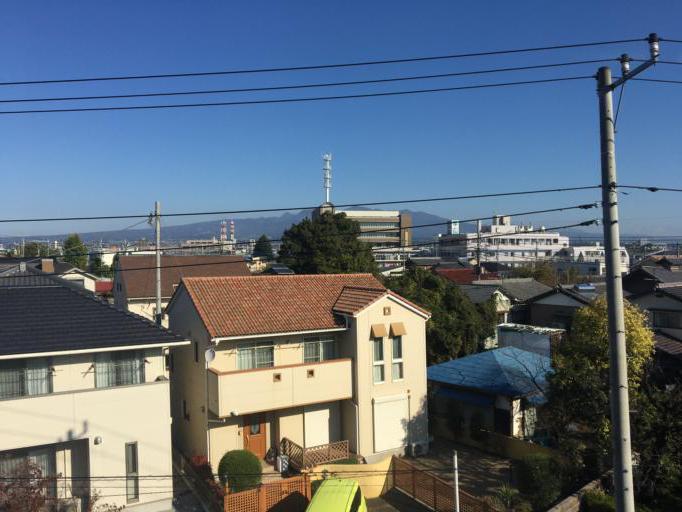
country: JP
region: Gunma
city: Maebashi-shi
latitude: 36.3818
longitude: 139.0890
